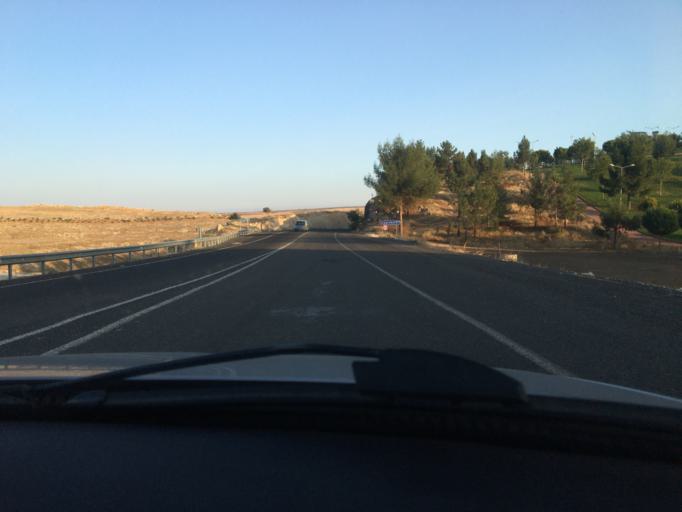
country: TR
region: Sanliurfa
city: Halfeti
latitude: 37.2292
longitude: 37.9517
